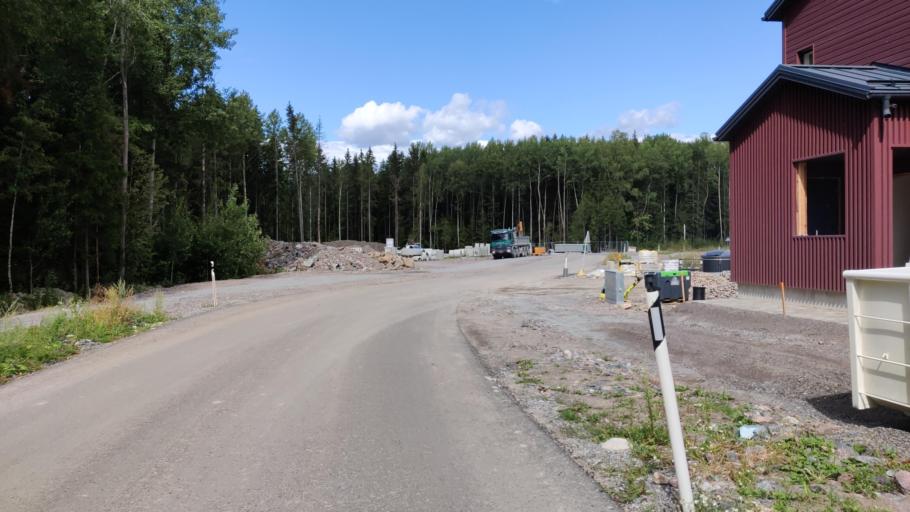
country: FI
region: Uusimaa
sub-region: Helsinki
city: Teekkarikylae
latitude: 60.2564
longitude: 24.8398
